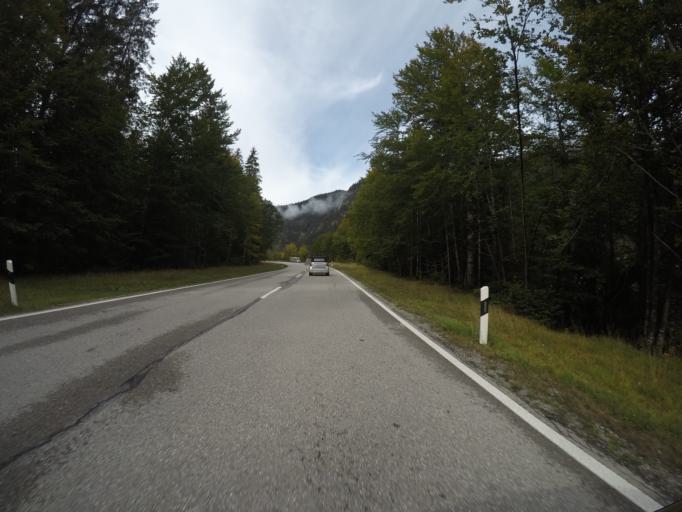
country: DE
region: Bavaria
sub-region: Upper Bavaria
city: Jachenau
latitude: 47.5587
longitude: 11.4648
